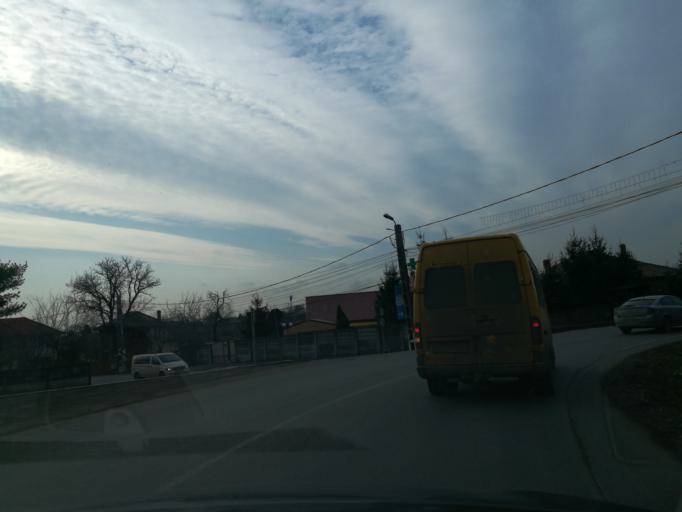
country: RO
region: Ilfov
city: Stefanestii de Jos
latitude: 44.5388
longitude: 26.2081
